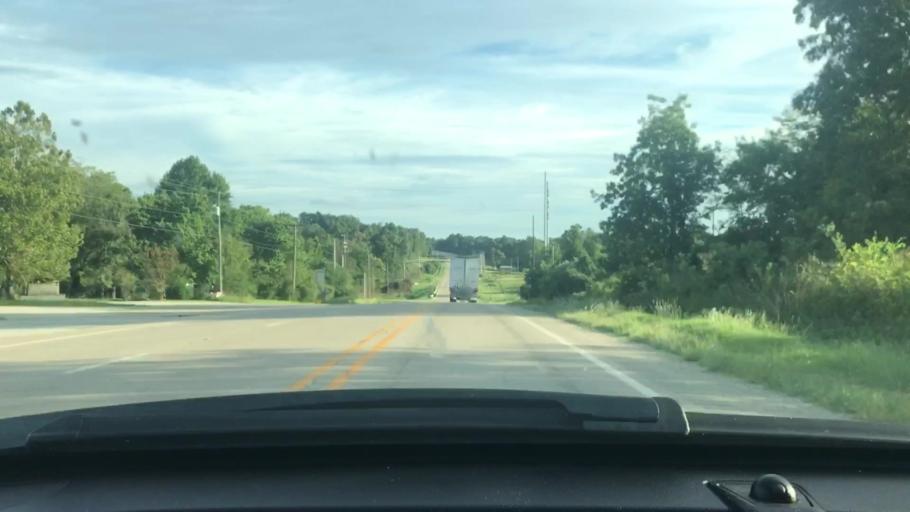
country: US
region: Arkansas
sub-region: Lawrence County
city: Hoxie
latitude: 36.1401
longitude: -91.1581
